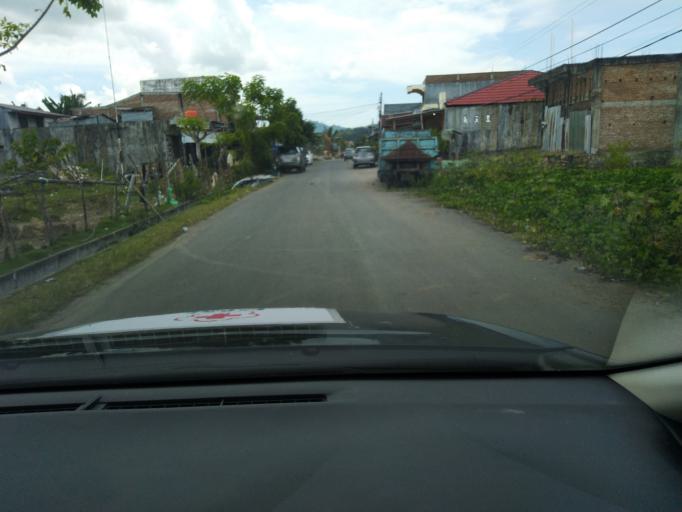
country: ID
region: Sulawesi Barat
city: Mamuju
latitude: -2.6821
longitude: 118.8794
